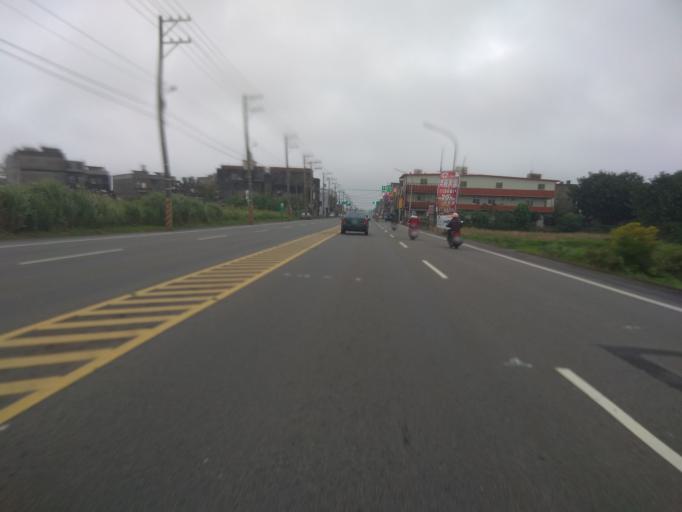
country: TW
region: Taiwan
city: Taoyuan City
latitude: 25.0245
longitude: 121.1141
